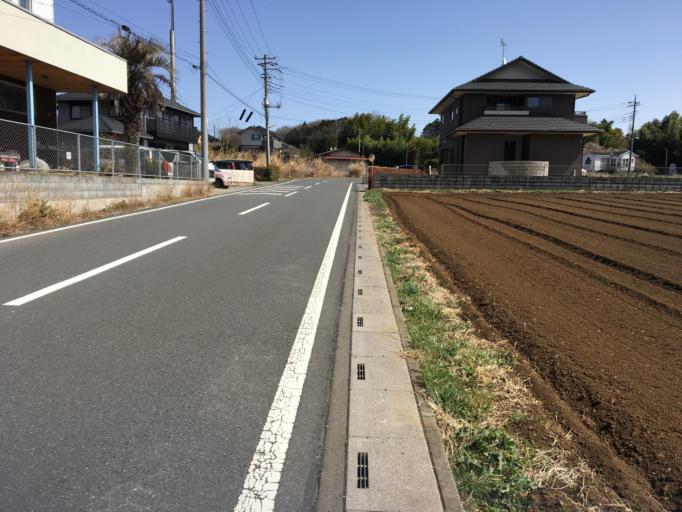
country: JP
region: Saitama
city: Sakado
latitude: 35.9931
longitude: 139.3354
